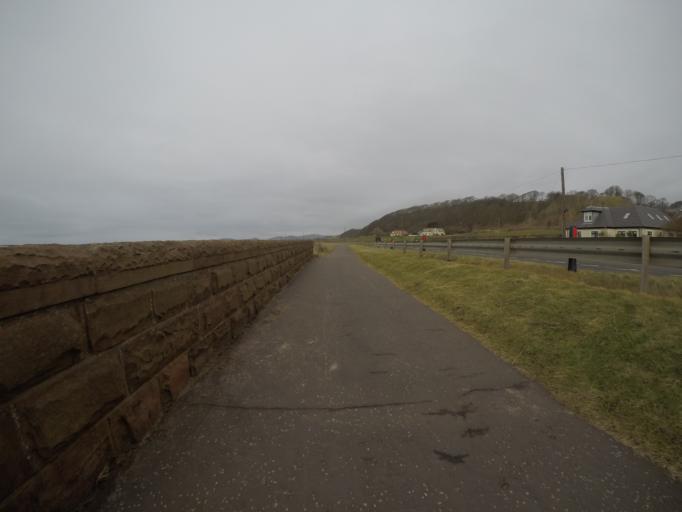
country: GB
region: Scotland
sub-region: North Ayrshire
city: West Kilbride
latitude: 55.6670
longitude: -4.8410
